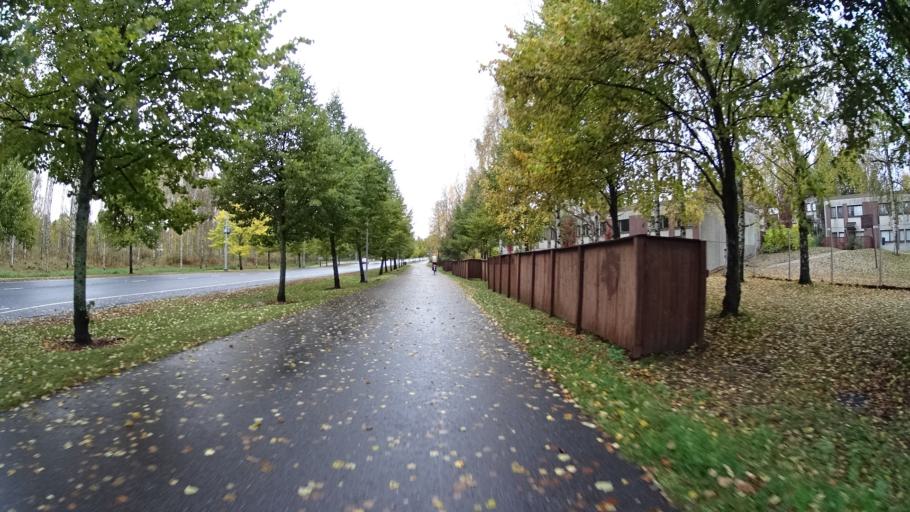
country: FI
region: Uusimaa
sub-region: Helsinki
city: Kilo
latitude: 60.2662
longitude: 24.8157
